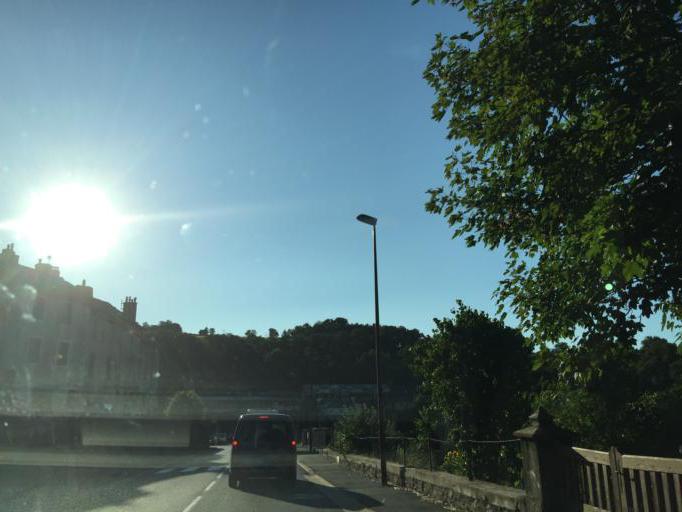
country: FR
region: Midi-Pyrenees
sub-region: Departement de l'Aveyron
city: Salles-Curan
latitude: 44.1832
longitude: 2.7880
